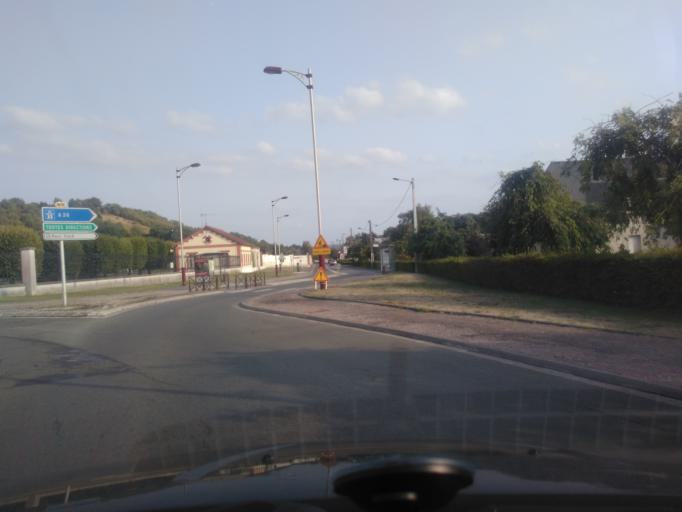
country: FR
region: Picardie
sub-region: Departement de l'Aisne
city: Laon
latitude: 49.5574
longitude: 3.6023
